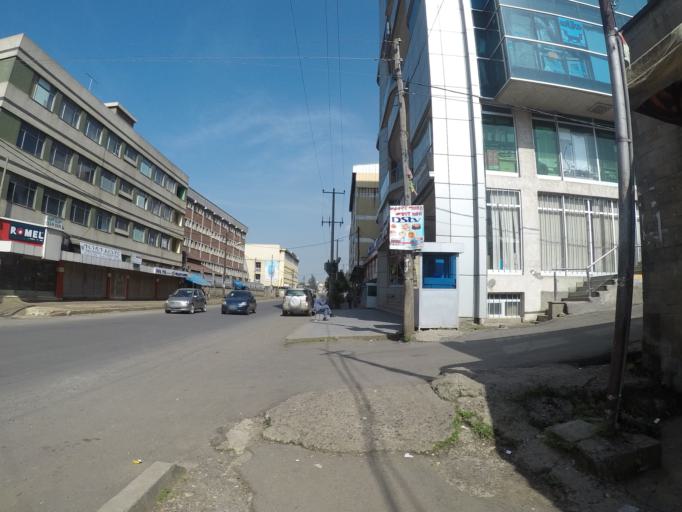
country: ET
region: Adis Abeba
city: Addis Ababa
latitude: 9.0311
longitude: 38.7502
